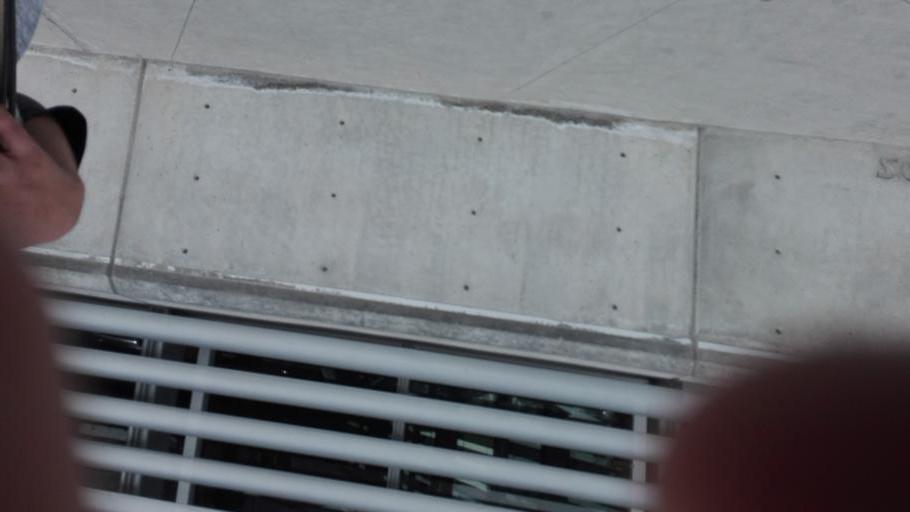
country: MX
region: Chihuahua
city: Ciudad Juarez
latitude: 31.7451
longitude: -106.4842
